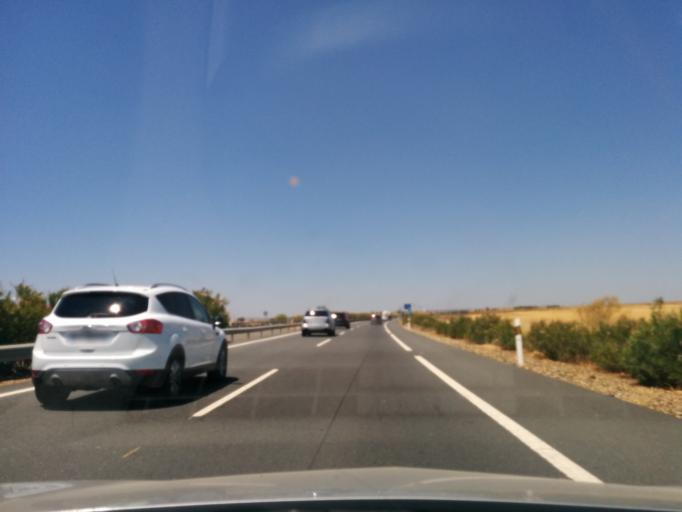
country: ES
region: Andalusia
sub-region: Provincia de Huelva
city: San Juan del Puerto
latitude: 37.3170
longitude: -6.9006
